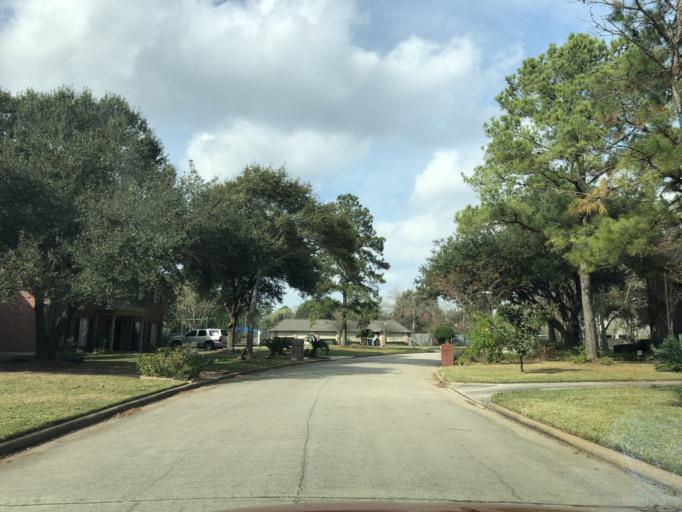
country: US
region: Texas
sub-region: Harris County
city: Tomball
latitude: 30.0347
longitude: -95.5422
